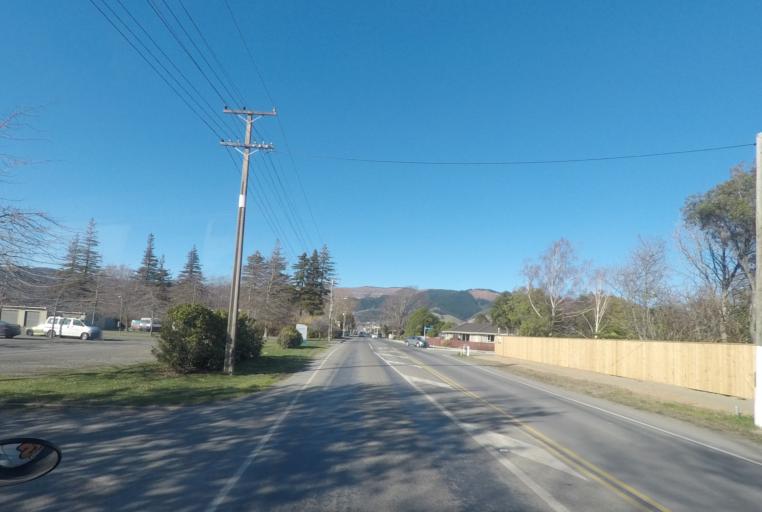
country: NZ
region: Tasman
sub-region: Tasman District
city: Richmond
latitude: -41.3314
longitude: 173.1761
